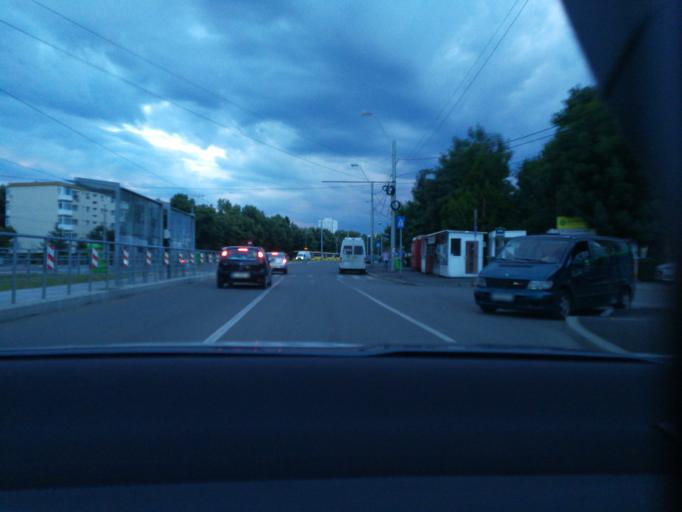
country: RO
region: Prahova
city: Ploiesti
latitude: 44.9311
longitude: 25.9894
